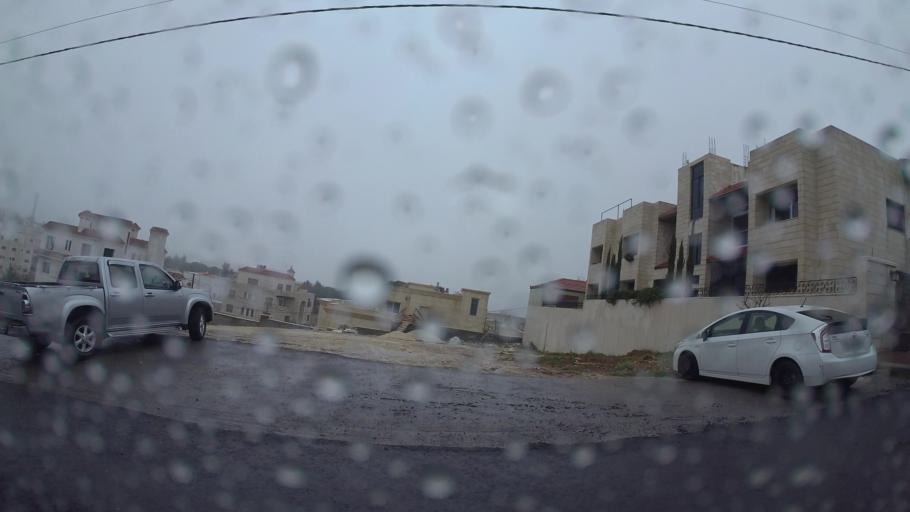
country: JO
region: Amman
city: Al Jubayhah
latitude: 32.0027
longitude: 35.8246
